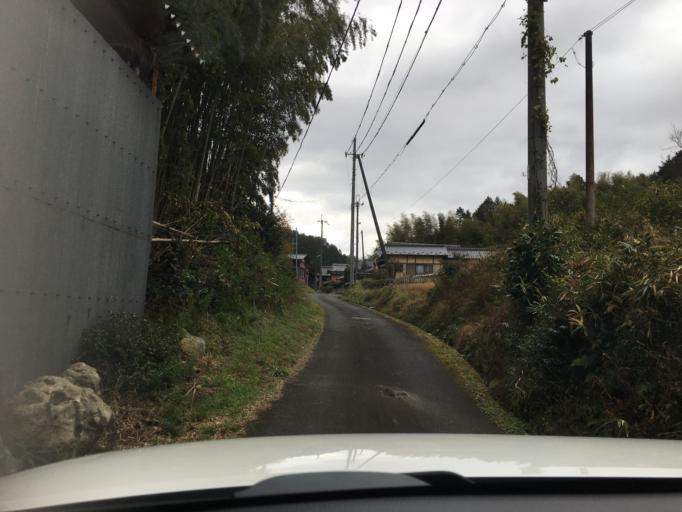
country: JP
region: Kyoto
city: Kameoka
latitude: 35.0411
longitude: 135.4759
